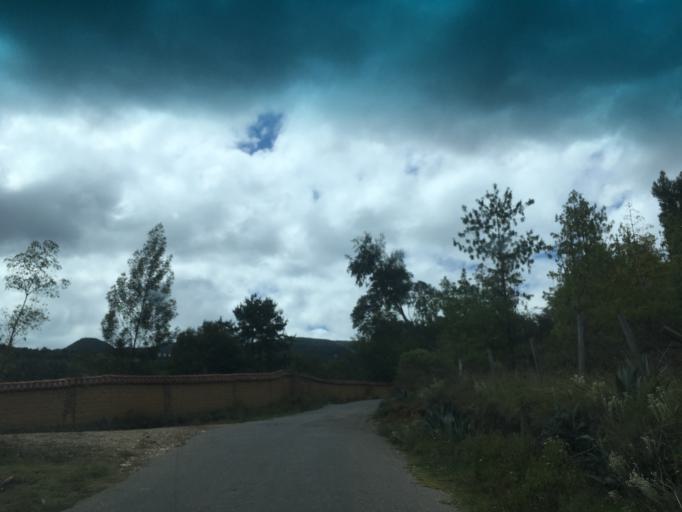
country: CO
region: Boyaca
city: Tibasosa
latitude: 5.7416
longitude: -73.0053
